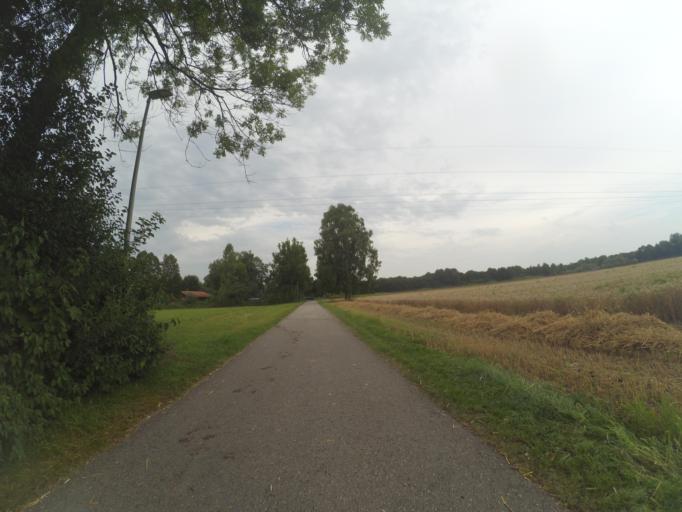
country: DE
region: Bavaria
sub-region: Swabia
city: Buchloe
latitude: 48.0233
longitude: 10.7184
